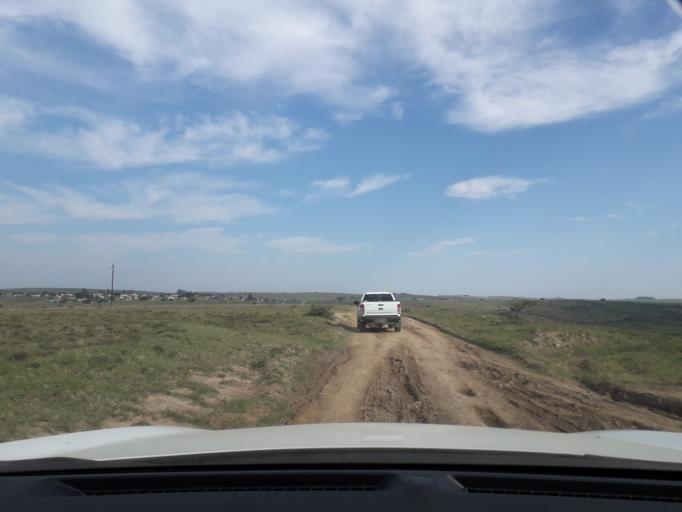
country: ZA
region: Eastern Cape
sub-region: Buffalo City Metropolitan Municipality
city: Bhisho
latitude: -32.9929
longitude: 27.3477
